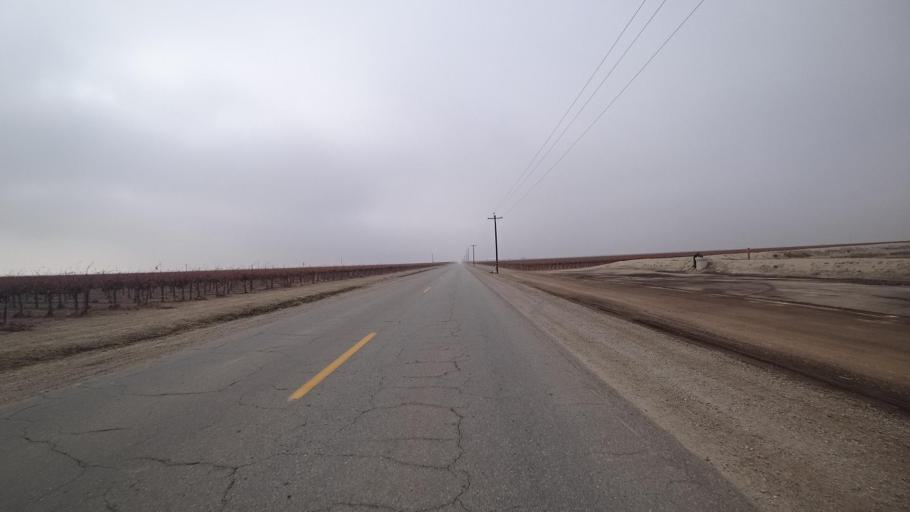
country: US
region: California
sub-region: Kern County
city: Maricopa
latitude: 35.0941
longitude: -119.1856
